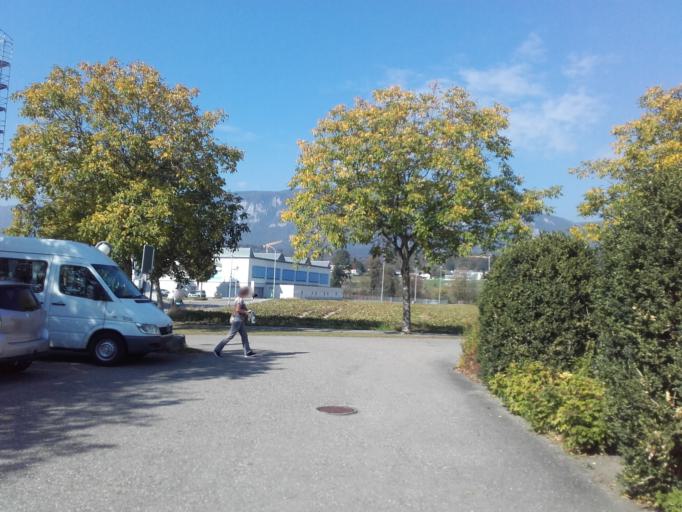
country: CH
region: Solothurn
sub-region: Bezirk Wasseramt
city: Zuchwil
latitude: 47.2145
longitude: 7.5621
